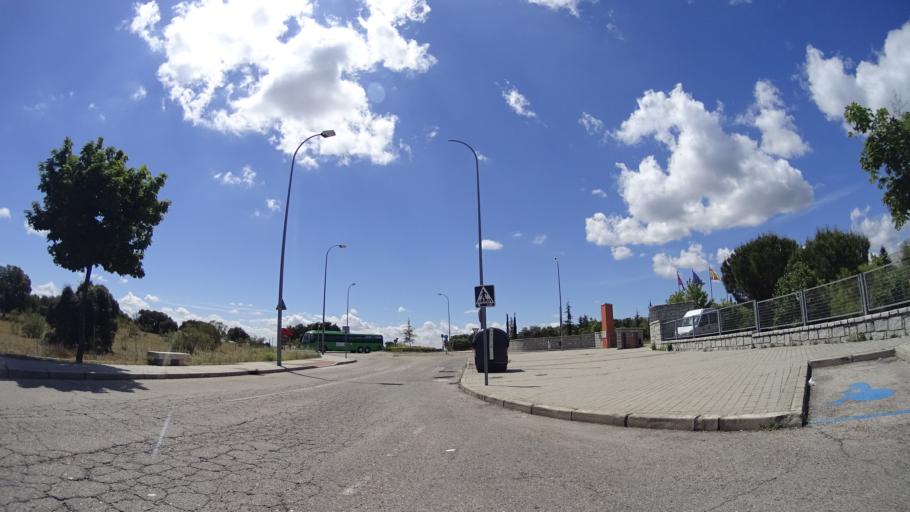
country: ES
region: Madrid
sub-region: Provincia de Madrid
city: Colmenarejo
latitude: 40.5430
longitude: -4.0111
